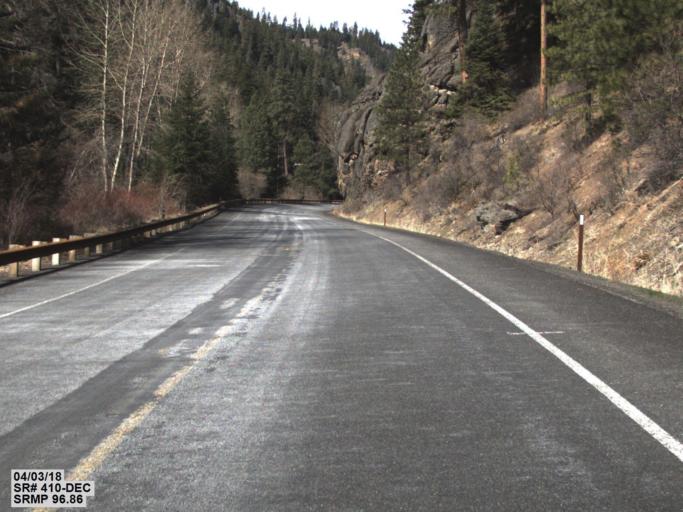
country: US
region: Washington
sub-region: Kittitas County
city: Cle Elum
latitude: 46.9334
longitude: -121.0554
